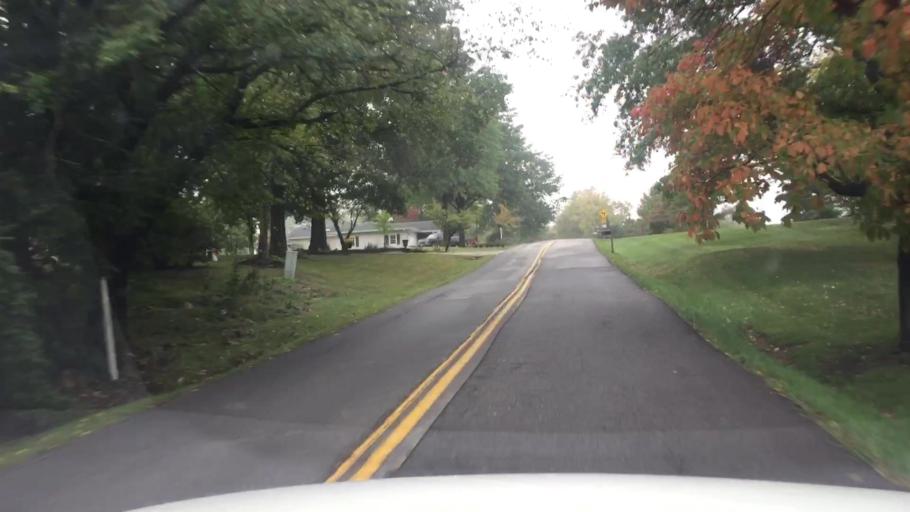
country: US
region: Missouri
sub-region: Boone County
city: Columbia
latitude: 38.8586
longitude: -92.3150
